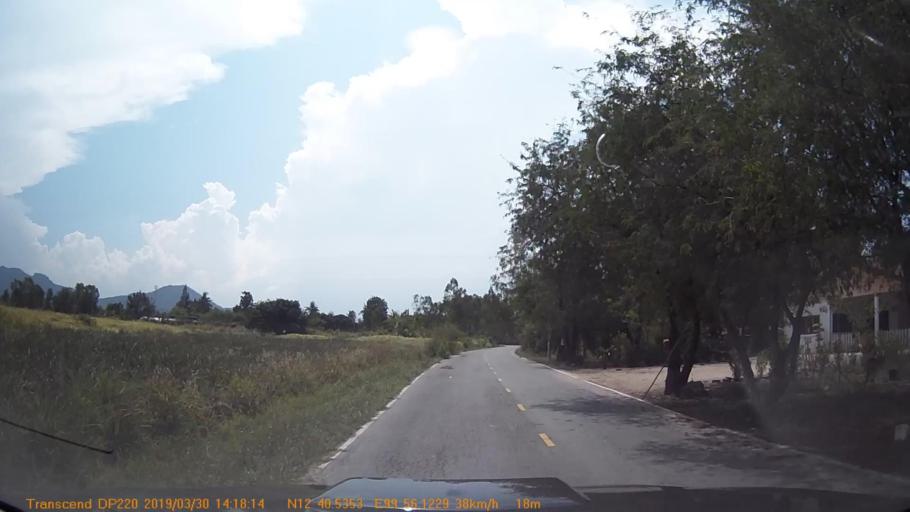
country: TH
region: Prachuap Khiri Khan
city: Hua Hin
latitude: 12.6756
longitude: 99.9352
